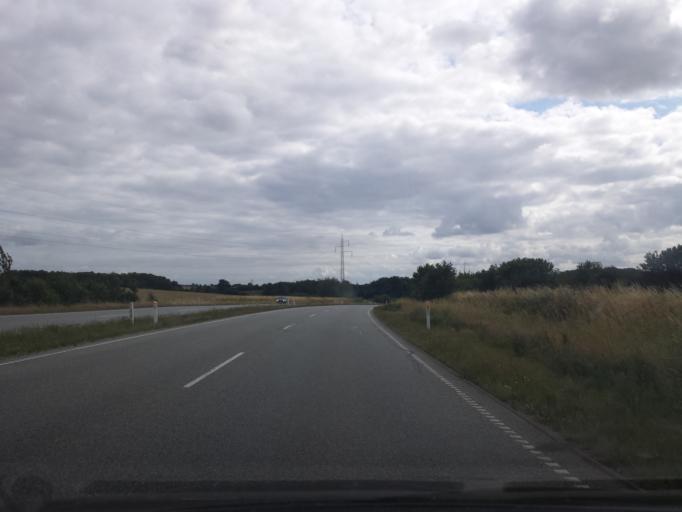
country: DK
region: South Denmark
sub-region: Sonderborg Kommune
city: Augustenborg
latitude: 54.9505
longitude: 9.8979
